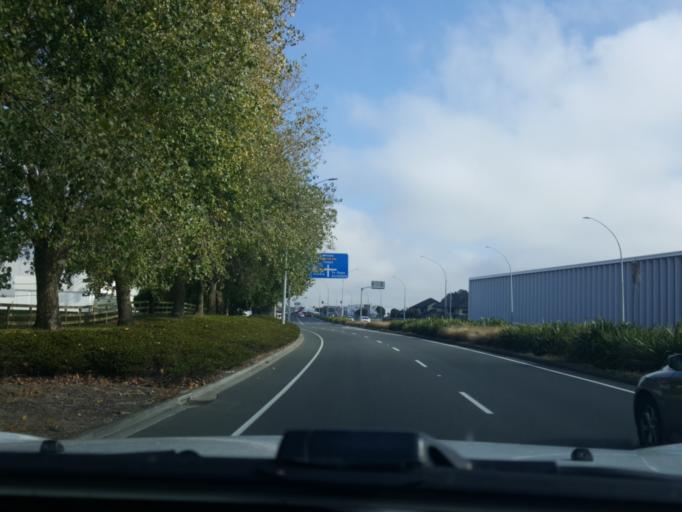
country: NZ
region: Waikato
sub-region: Hamilton City
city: Hamilton
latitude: -37.7482
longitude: 175.2400
